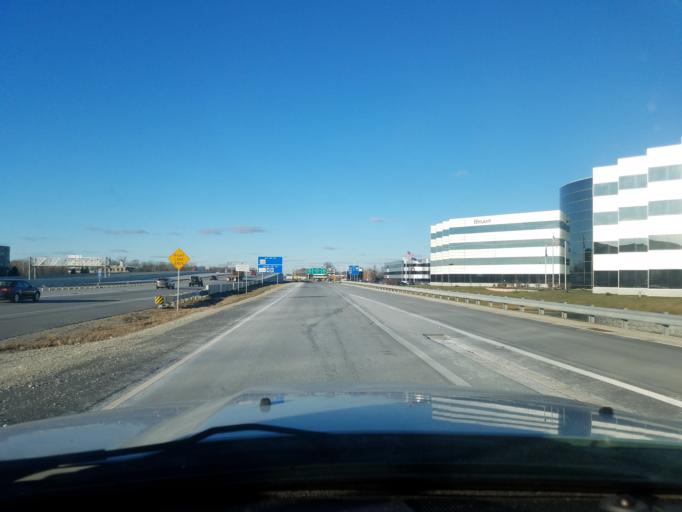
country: US
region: Indiana
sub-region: Marion County
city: Meridian Hills
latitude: 39.9393
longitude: -86.1574
